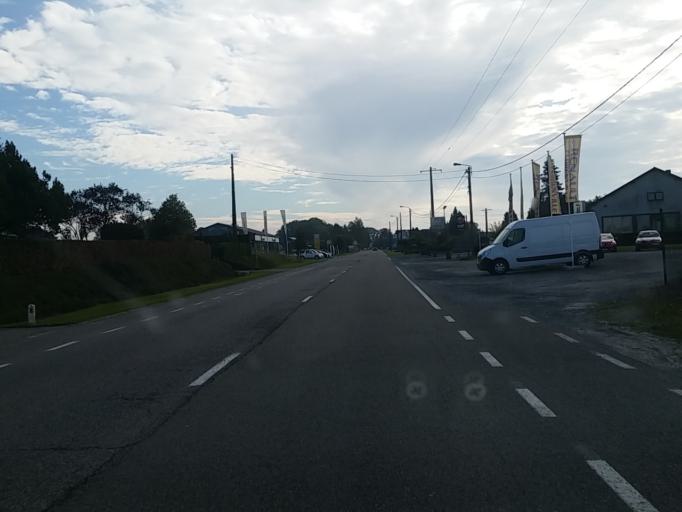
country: BE
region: Wallonia
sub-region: Province du Luxembourg
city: Florenville
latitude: 49.6980
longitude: 5.2932
